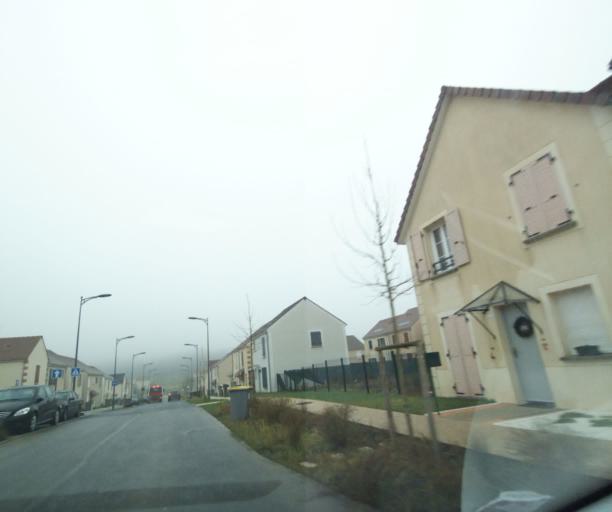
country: FR
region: Ile-de-France
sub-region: Departement de Seine-et-Marne
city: Othis
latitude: 49.0638
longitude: 2.6748
